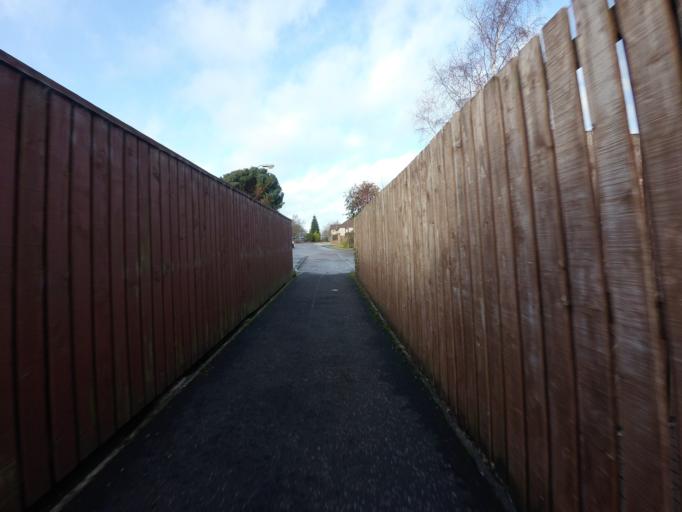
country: GB
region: Scotland
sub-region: West Lothian
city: West Calder
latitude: 55.8787
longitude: -3.5838
